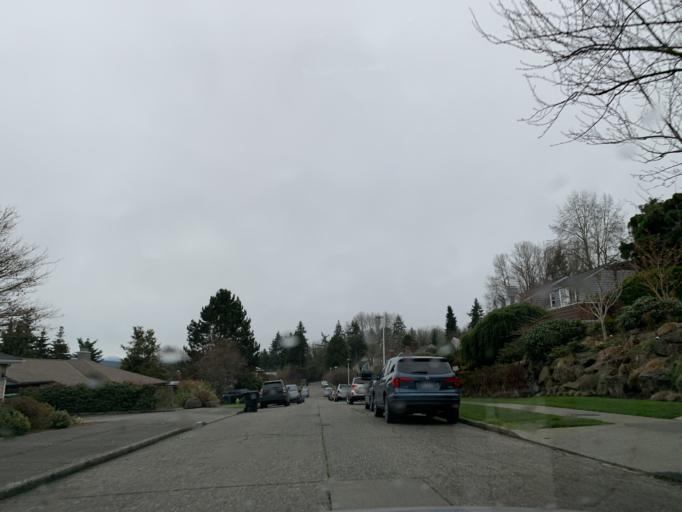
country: US
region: Washington
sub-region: King County
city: Yarrow Point
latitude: 47.6665
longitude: -122.2718
